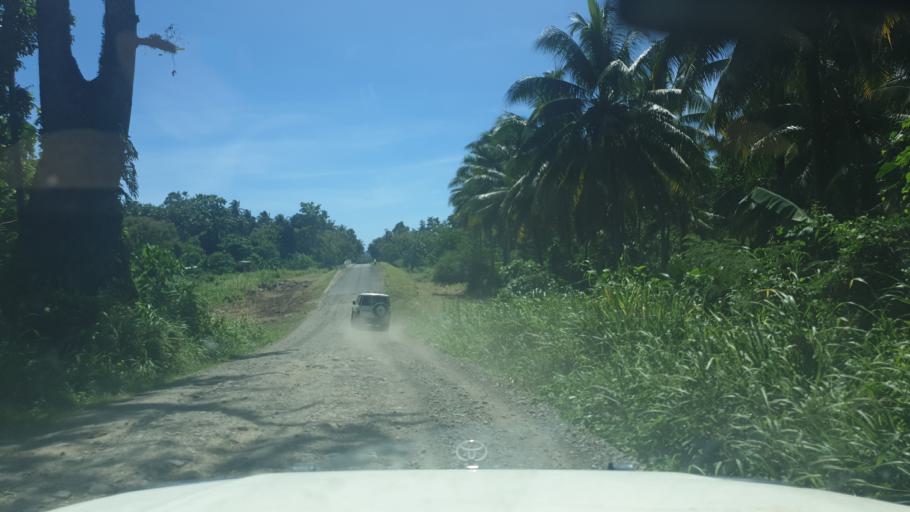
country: PG
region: Bougainville
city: Buka
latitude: -5.6613
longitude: 155.0969
